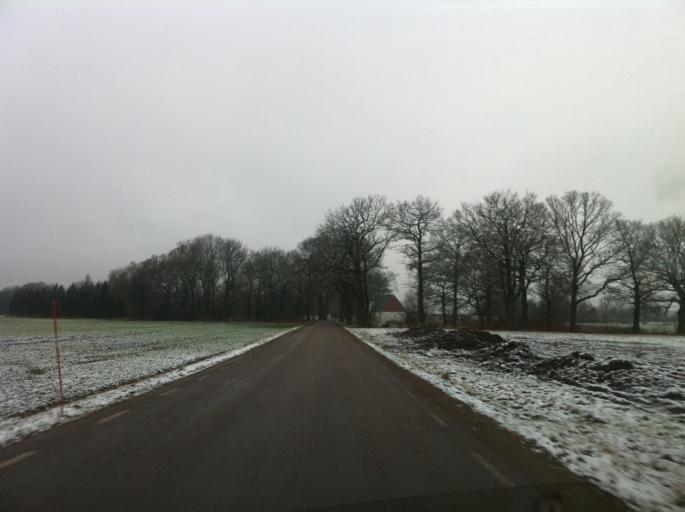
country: SE
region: Skane
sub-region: Bjuvs Kommun
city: Billesholm
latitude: 55.9779
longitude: 13.0152
